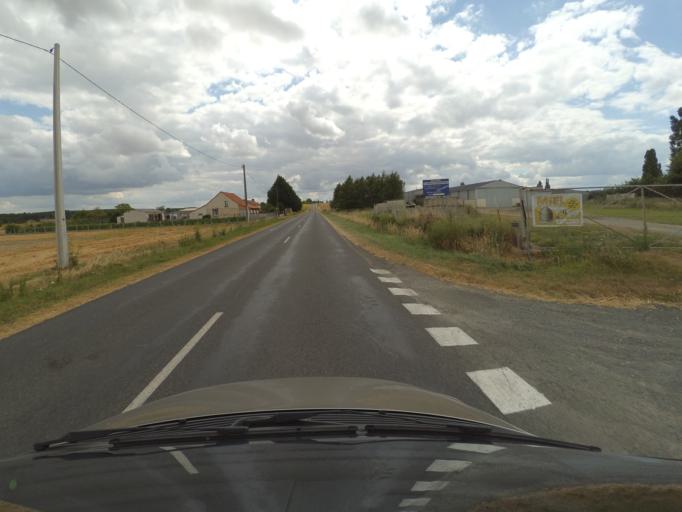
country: FR
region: Centre
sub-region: Departement d'Indre-et-Loire
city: Richelieu
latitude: 46.9674
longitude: 0.3757
